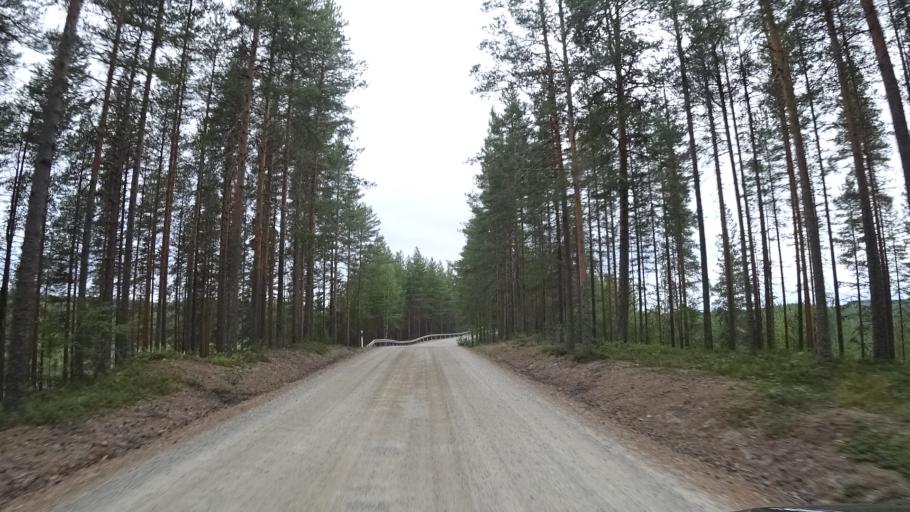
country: FI
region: North Karelia
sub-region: Pielisen Karjala
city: Lieksa
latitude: 63.2341
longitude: 30.3655
